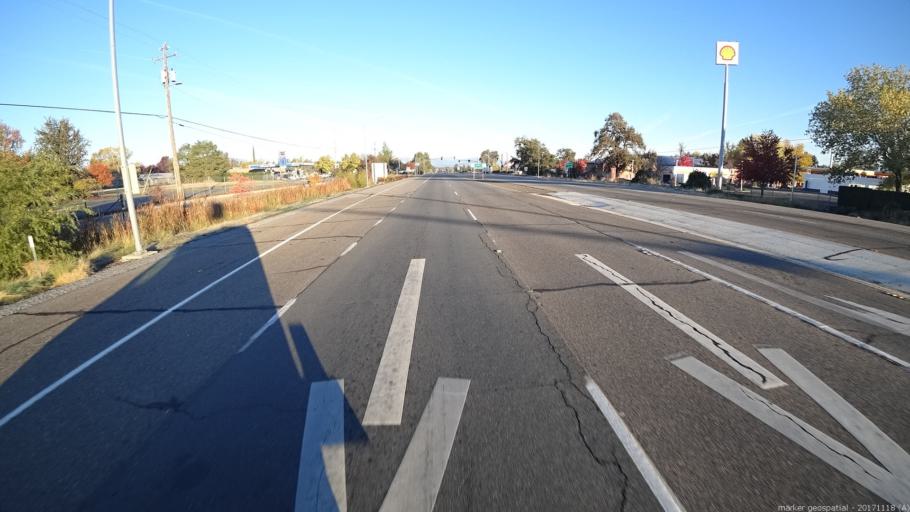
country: US
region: California
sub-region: Shasta County
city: Anderson
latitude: 40.4372
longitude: -122.2904
